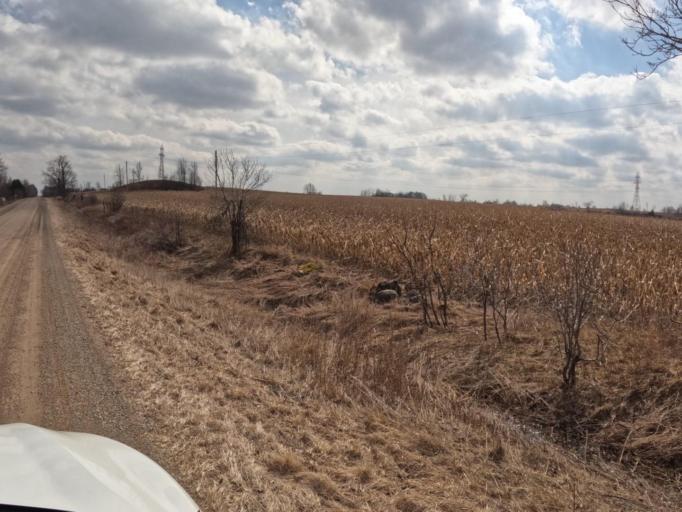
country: CA
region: Ontario
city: Shelburne
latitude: 43.9581
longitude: -80.2812
